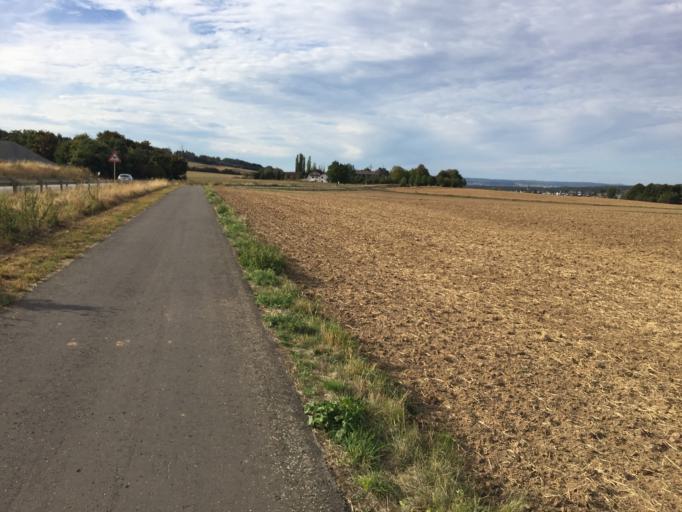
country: DE
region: Hesse
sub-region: Regierungsbezirk Giessen
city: Langgons
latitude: 50.5155
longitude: 8.7252
